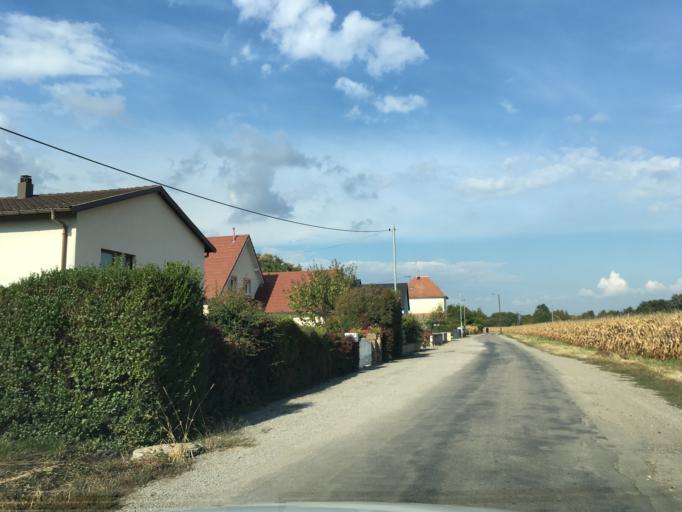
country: FR
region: Alsace
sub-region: Departement du Haut-Rhin
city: Colmar
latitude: 48.0713
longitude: 7.3770
